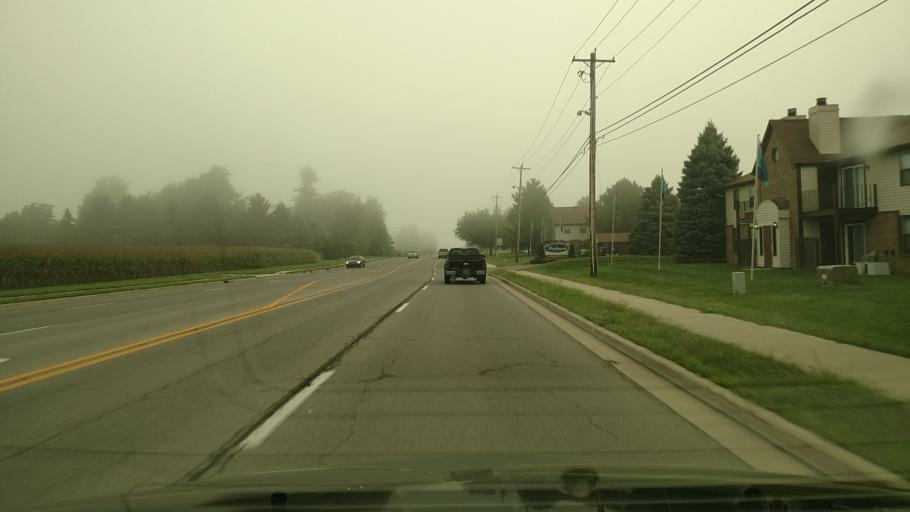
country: US
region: Indiana
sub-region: Howard County
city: Indian Heights
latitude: 40.4475
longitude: -86.1651
